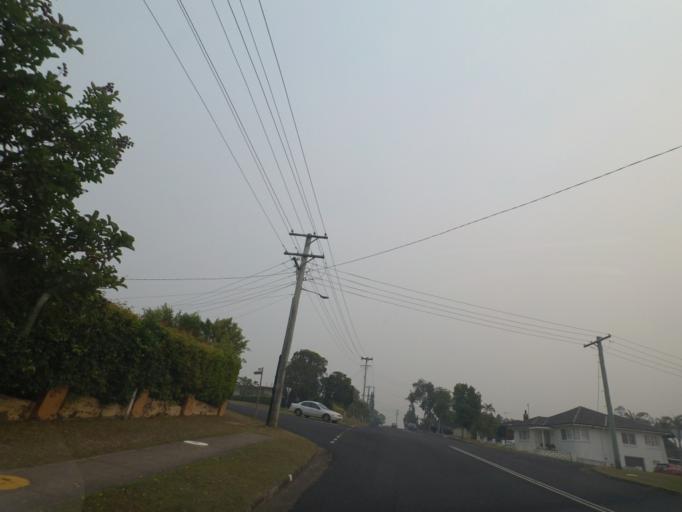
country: AU
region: New South Wales
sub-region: Coffs Harbour
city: Coffs Harbour
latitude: -30.2907
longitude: 153.1075
